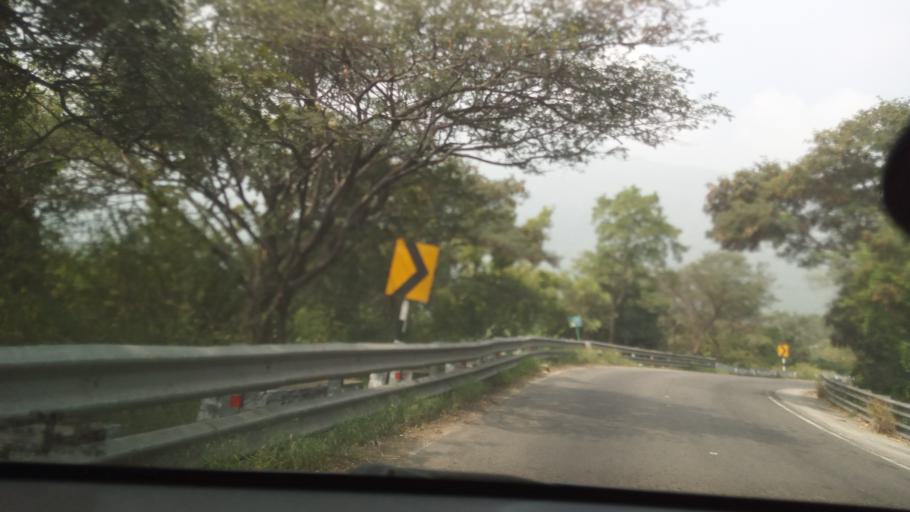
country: IN
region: Tamil Nadu
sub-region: Erode
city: Sathyamangalam
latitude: 11.5900
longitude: 77.1287
